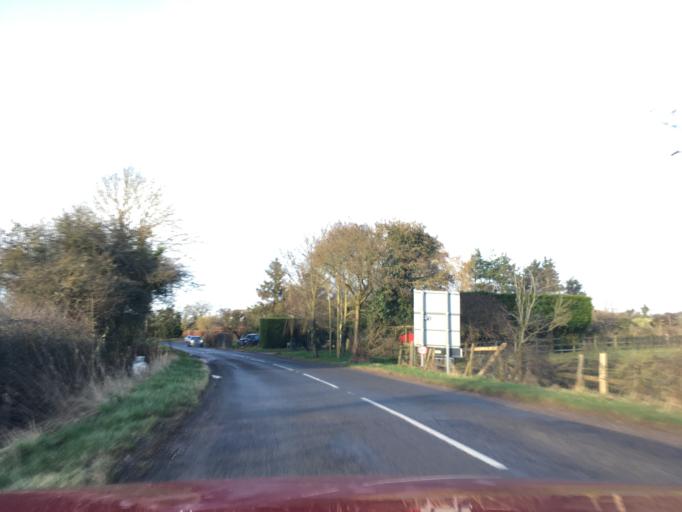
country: GB
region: England
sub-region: Warwickshire
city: Henley in Arden
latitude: 52.2495
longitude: -1.7947
